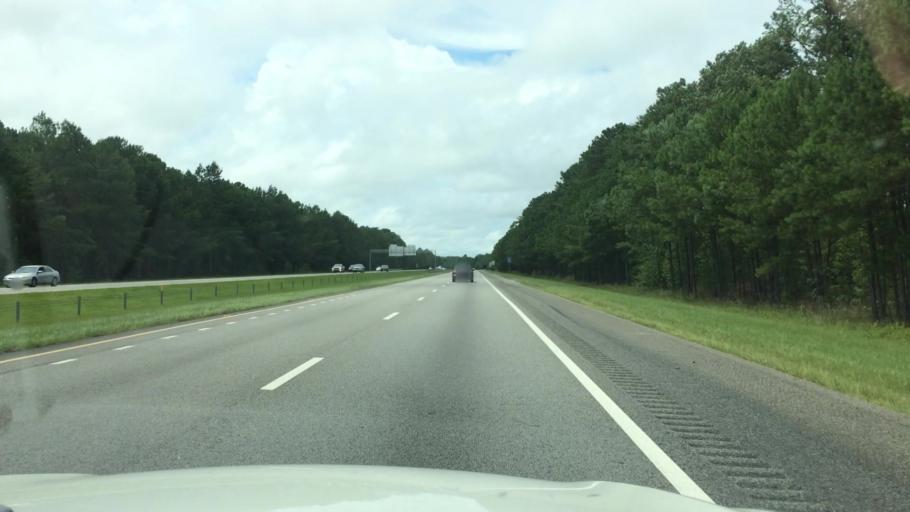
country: US
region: South Carolina
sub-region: Florence County
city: Florence
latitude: 34.1993
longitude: -79.8569
